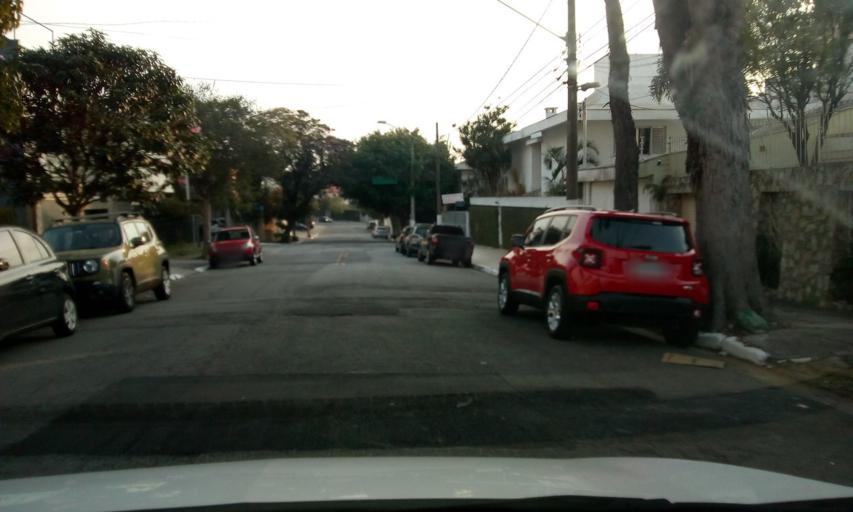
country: BR
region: Sao Paulo
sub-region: Sao Paulo
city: Sao Paulo
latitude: -23.6178
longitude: -46.6493
